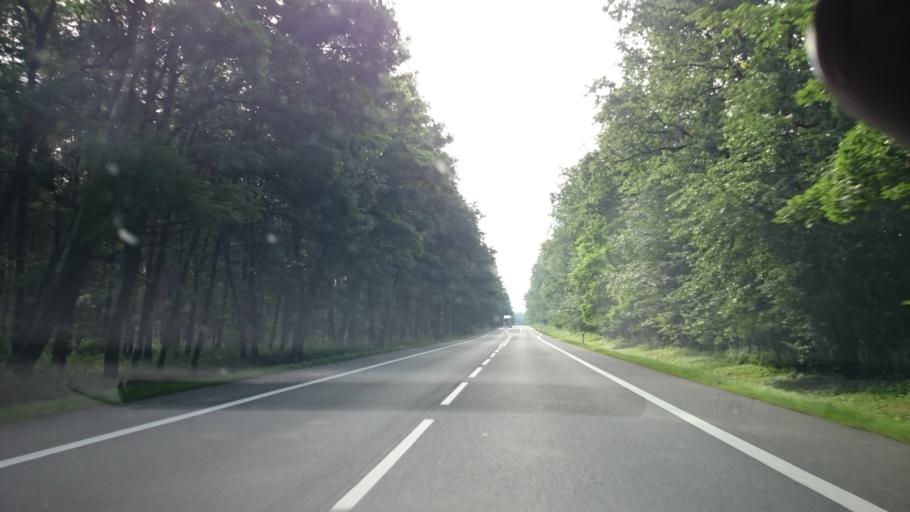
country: PL
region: Opole Voivodeship
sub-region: Powiat opolski
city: Chrzastowice
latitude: 50.6265
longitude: 18.0397
